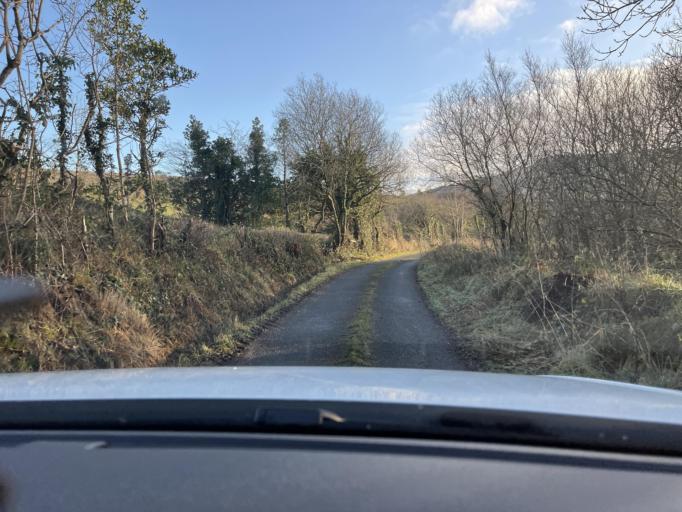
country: IE
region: Connaught
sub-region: County Leitrim
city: Manorhamilton
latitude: 54.2120
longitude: -7.9684
